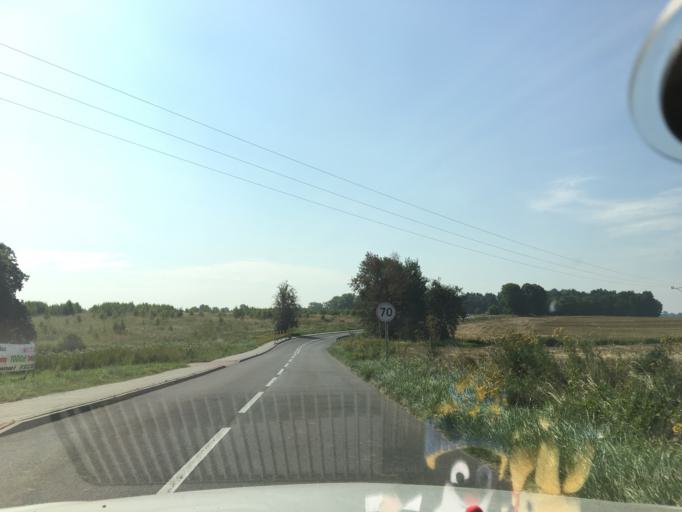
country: PL
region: West Pomeranian Voivodeship
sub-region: Powiat gryficki
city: Pobierowo
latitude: 54.0380
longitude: 14.8740
